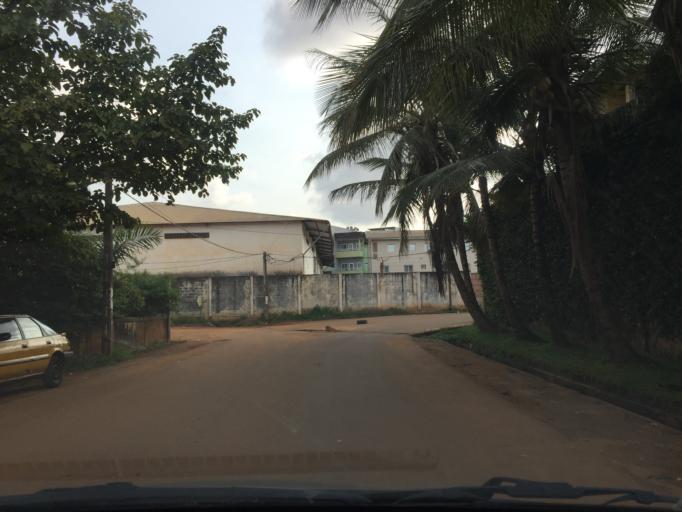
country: CM
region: Centre
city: Yaounde
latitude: 3.8834
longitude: 11.5145
